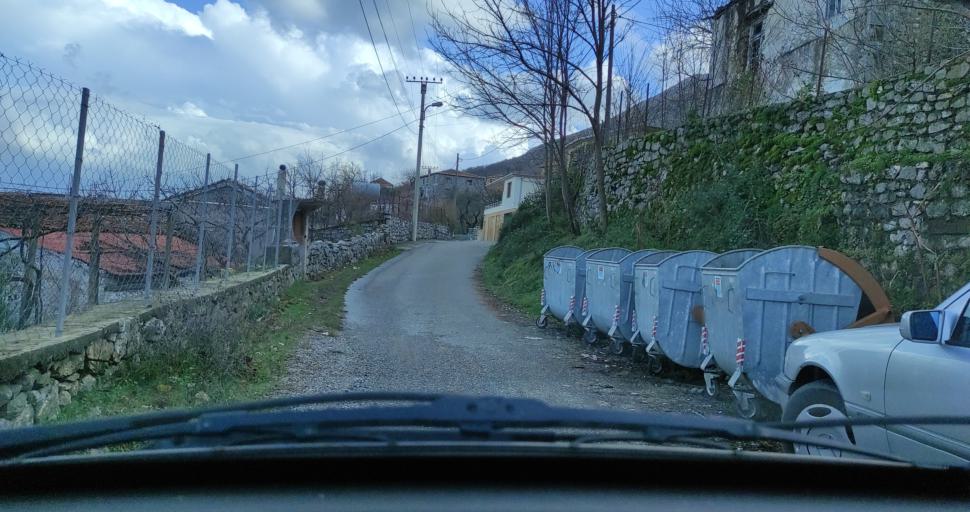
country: AL
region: Shkoder
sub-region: Rrethi i Shkodres
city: Dajc
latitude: 42.0713
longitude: 19.3992
